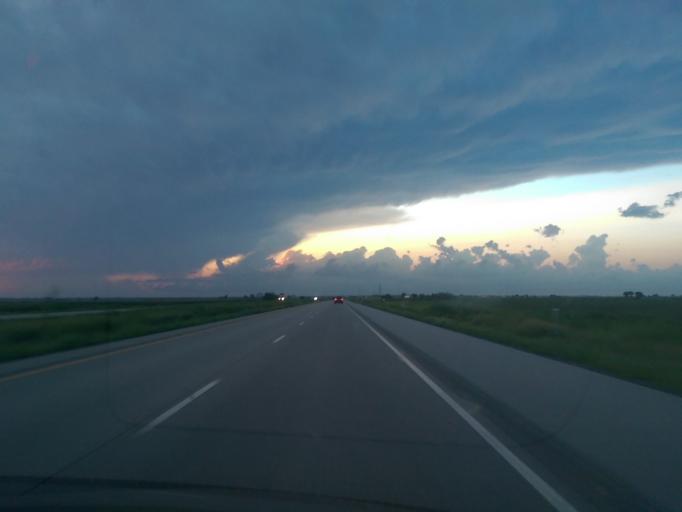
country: US
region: Nebraska
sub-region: Otoe County
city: Nebraska City
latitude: 40.7005
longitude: -95.7910
